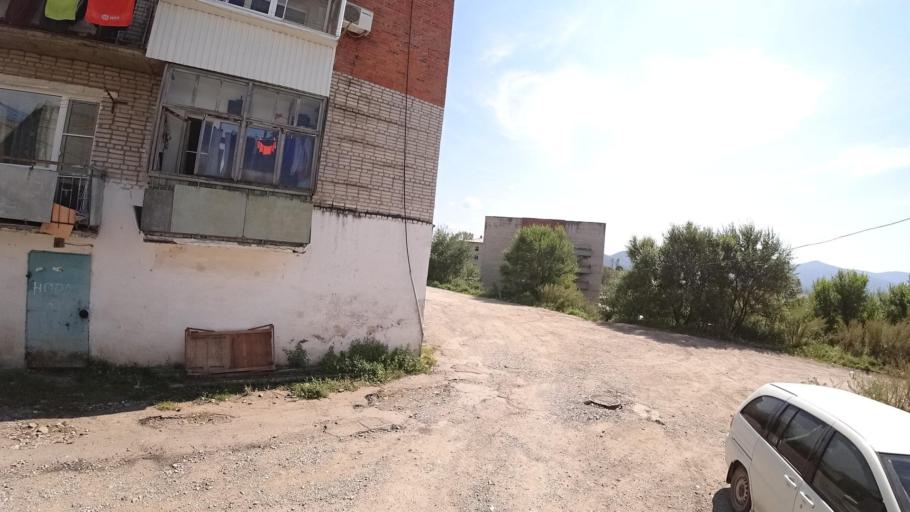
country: RU
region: Jewish Autonomous Oblast
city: Londoko
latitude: 49.0138
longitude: 131.8822
